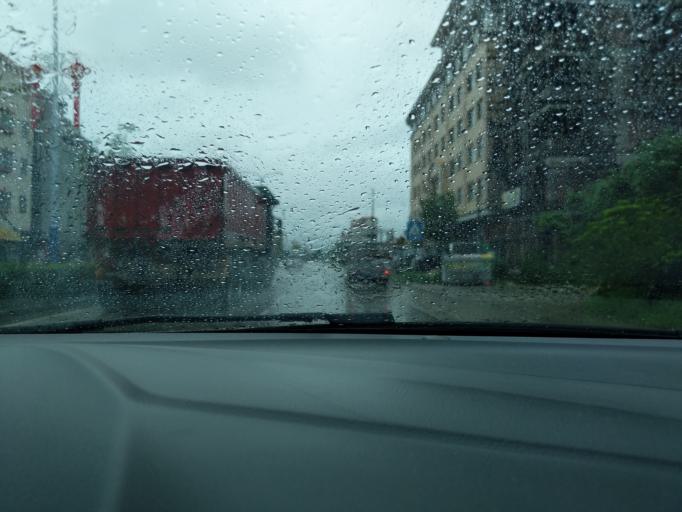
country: CN
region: Guangdong
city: Pingshi
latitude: 22.2060
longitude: 112.3258
